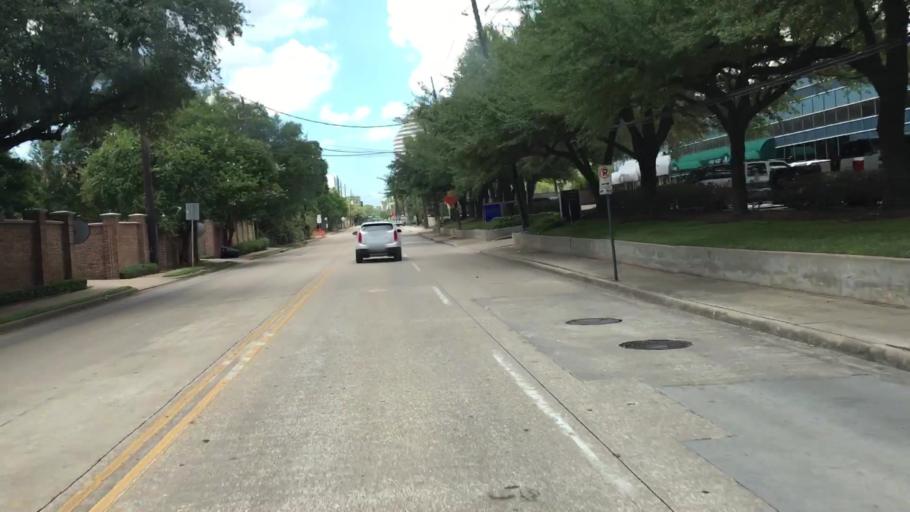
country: US
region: Texas
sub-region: Harris County
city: Hunters Creek Village
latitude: 29.7532
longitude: -95.4630
